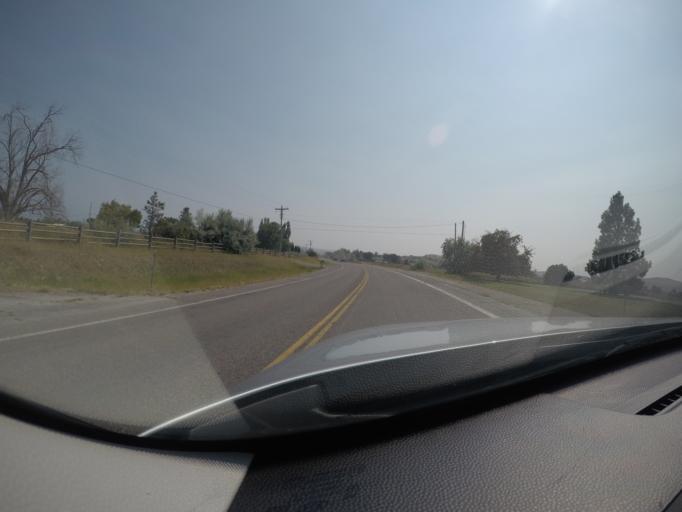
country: US
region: Montana
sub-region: Lake County
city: Polson
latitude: 47.7153
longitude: -114.1886
